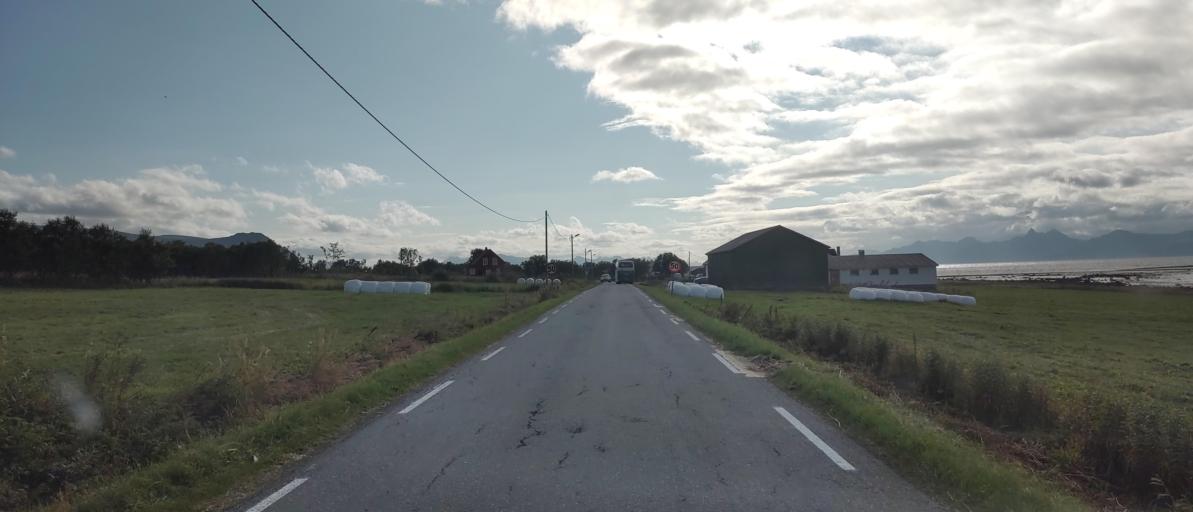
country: NO
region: Nordland
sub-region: Sortland
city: Sortland
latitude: 69.0491
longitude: 15.5213
